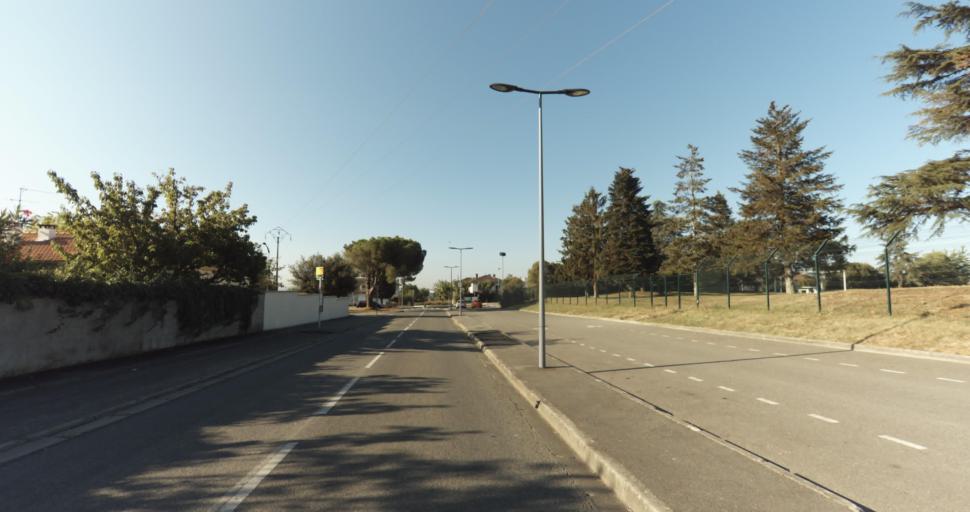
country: FR
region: Midi-Pyrenees
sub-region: Departement de la Haute-Garonne
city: L'Union
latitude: 43.6548
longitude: 1.4917
